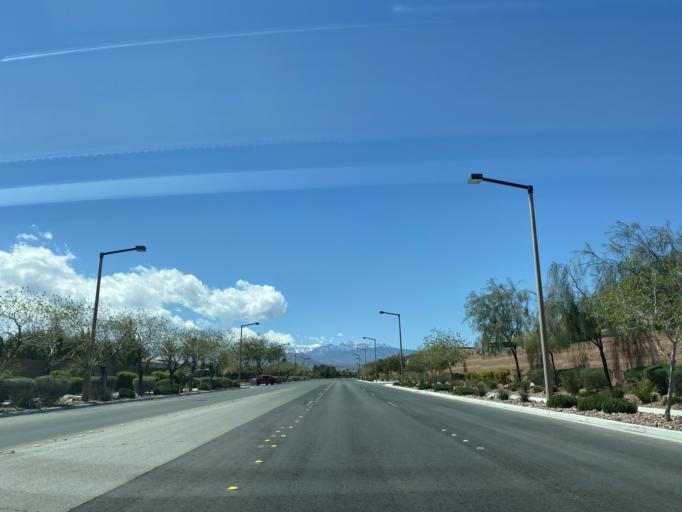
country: US
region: Nevada
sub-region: Clark County
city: North Las Vegas
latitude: 36.3128
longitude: -115.2208
